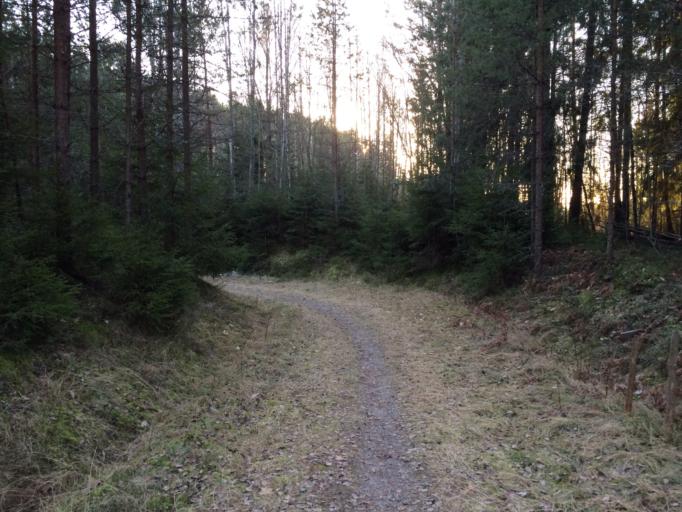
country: SE
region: Vaestmanland
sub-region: Hallstahammars Kommun
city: Hallstahammar
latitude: 59.6157
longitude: 16.1998
